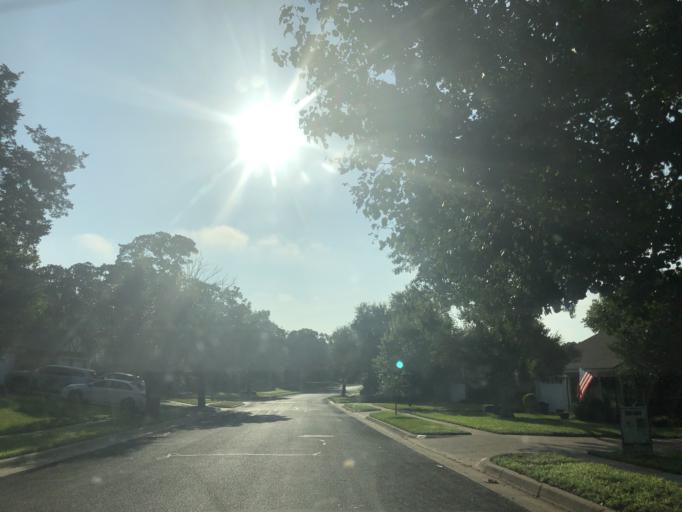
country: US
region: Texas
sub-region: Tarrant County
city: Euless
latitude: 32.8678
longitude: -97.0790
